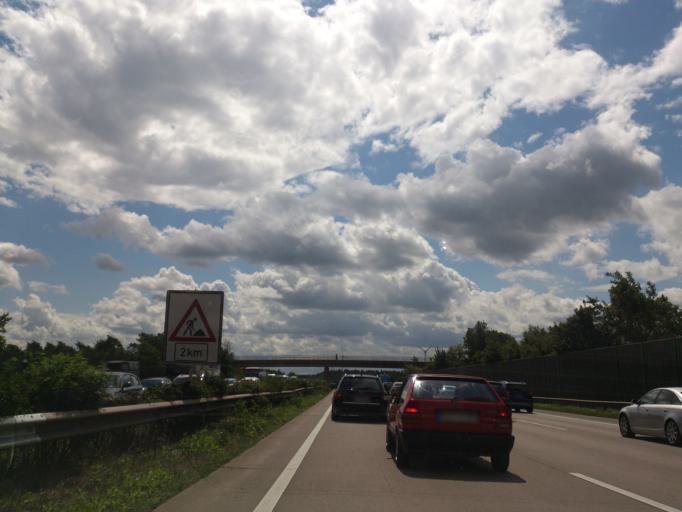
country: DE
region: Lower Saxony
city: Elze
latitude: 52.5976
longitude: 9.7486
